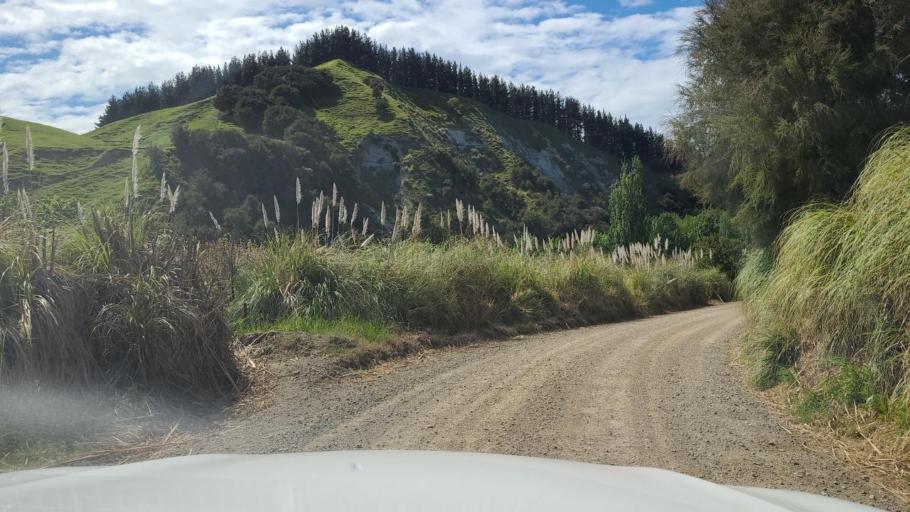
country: NZ
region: Hawke's Bay
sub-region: Napier City
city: Napier
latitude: -39.1383
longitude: 177.0157
